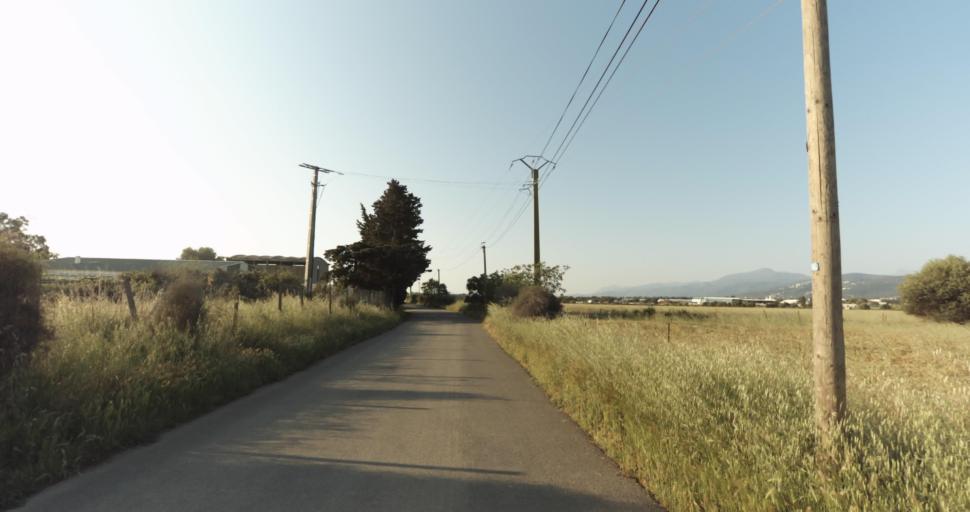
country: FR
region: Corsica
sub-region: Departement de la Haute-Corse
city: Biguglia
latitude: 42.6086
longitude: 9.4492
